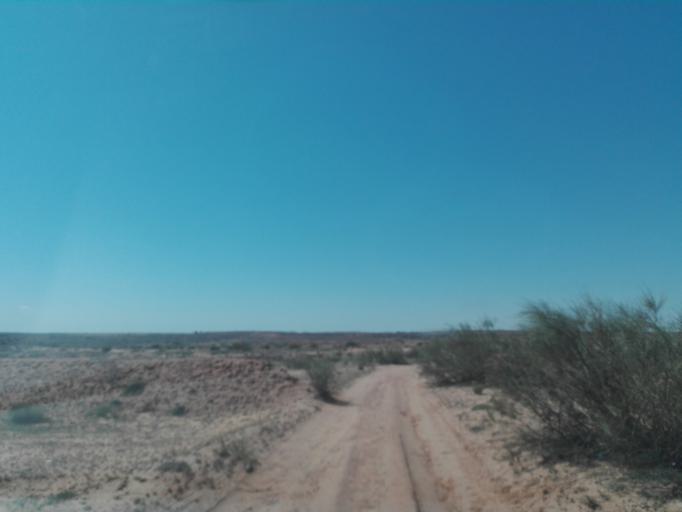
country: TN
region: Safaqis
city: Bi'r `Ali Bin Khalifah
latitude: 34.7928
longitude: 10.2809
